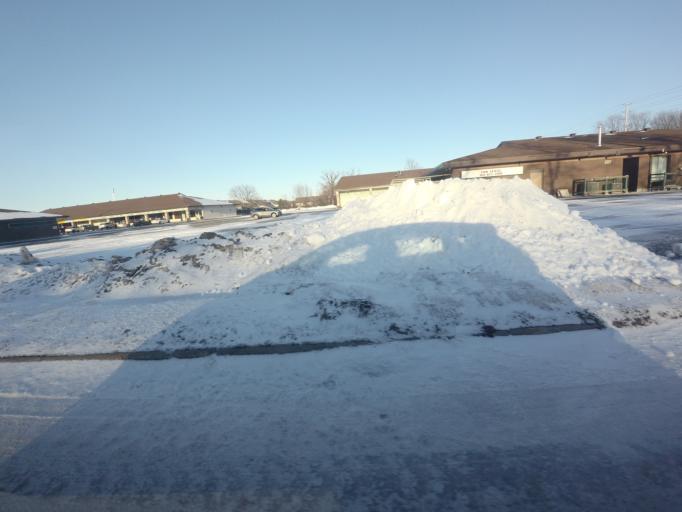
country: CA
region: Ontario
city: Bells Corners
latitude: 45.1930
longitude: -75.8424
